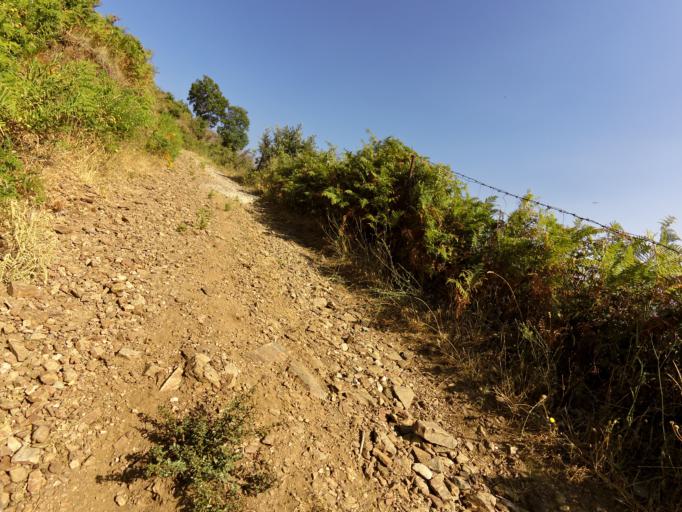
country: IT
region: Calabria
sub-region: Provincia di Reggio Calabria
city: Bivongi
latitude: 38.4989
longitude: 16.4535
